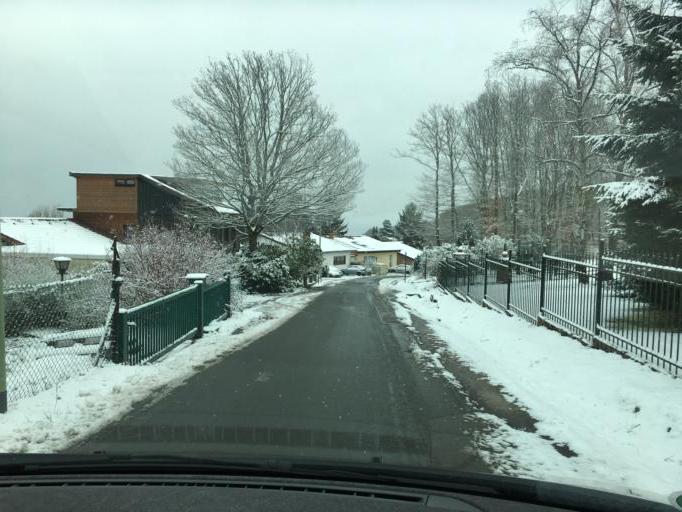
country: DE
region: North Rhine-Westphalia
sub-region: Regierungsbezirk Koln
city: Hurtgenwald
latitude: 50.7359
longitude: 6.4243
